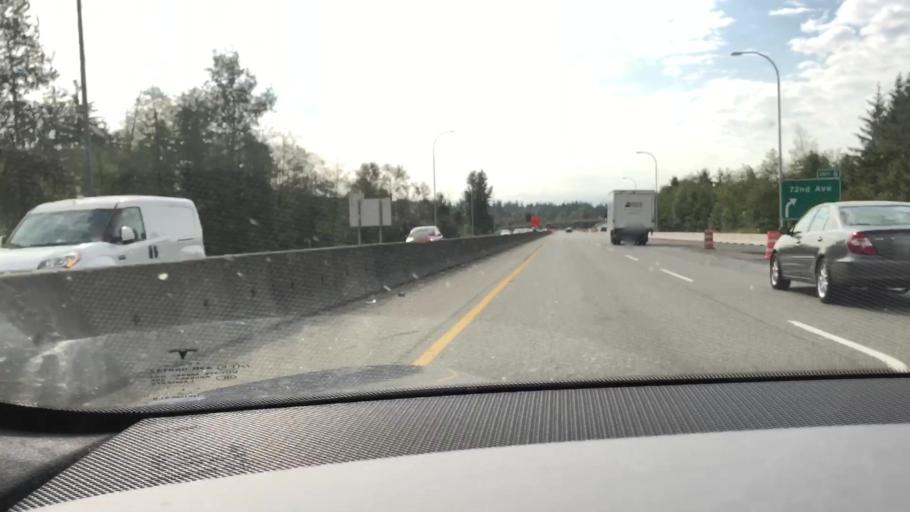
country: CA
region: British Columbia
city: Delta
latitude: 49.1385
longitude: -122.9329
